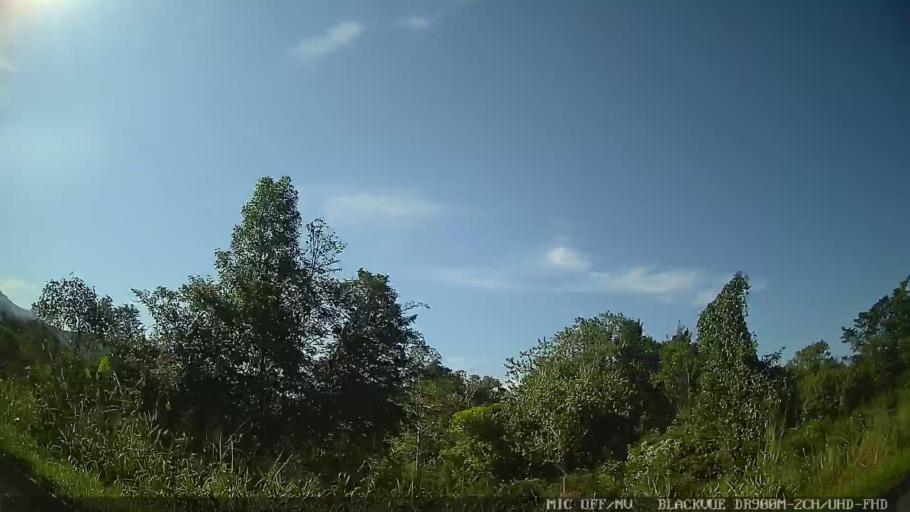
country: BR
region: Sao Paulo
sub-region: Santos
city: Santos
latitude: -23.8941
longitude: -46.2752
